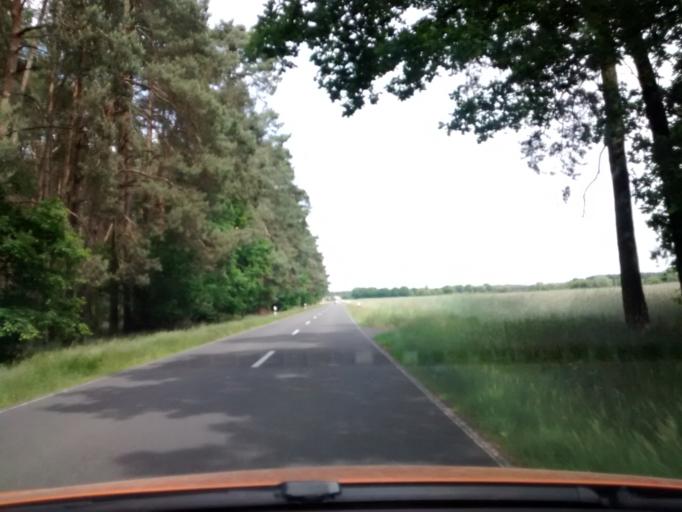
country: DE
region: Brandenburg
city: Ihlow
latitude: 51.8550
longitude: 13.2850
